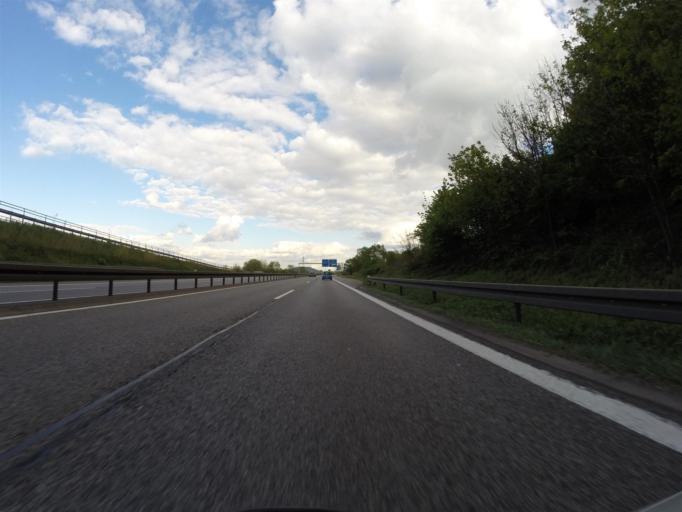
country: DE
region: Saarland
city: Wallerfangen
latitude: 49.3389
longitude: 6.7150
